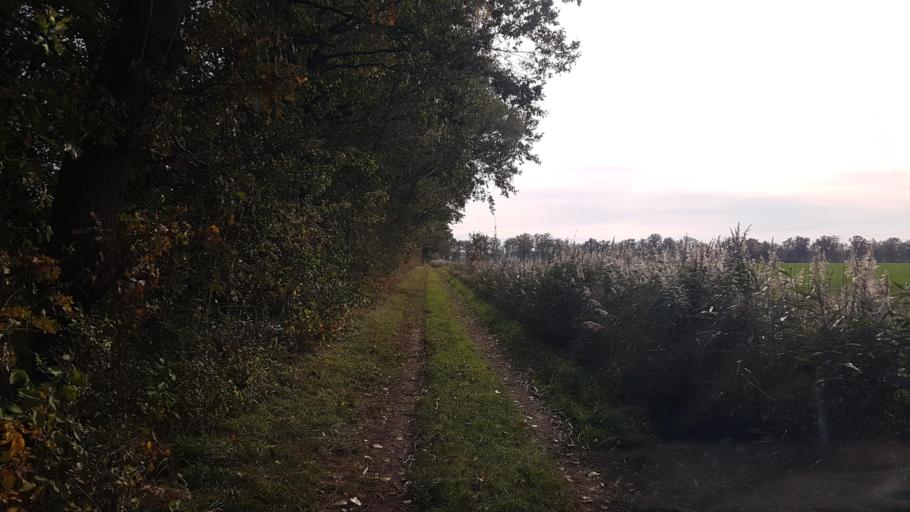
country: DE
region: Brandenburg
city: Schraden
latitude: 51.4571
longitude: 13.6992
